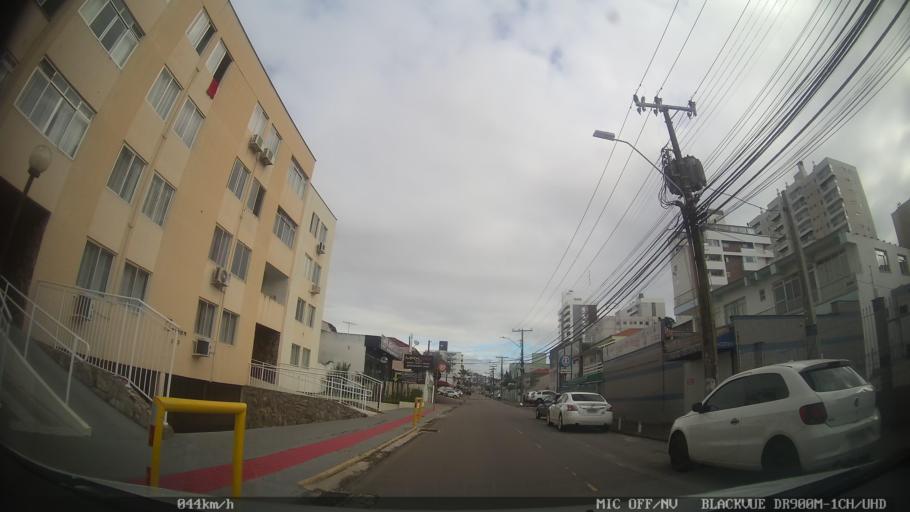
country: BR
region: Santa Catarina
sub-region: Sao Jose
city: Campinas
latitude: -27.5716
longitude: -48.6095
